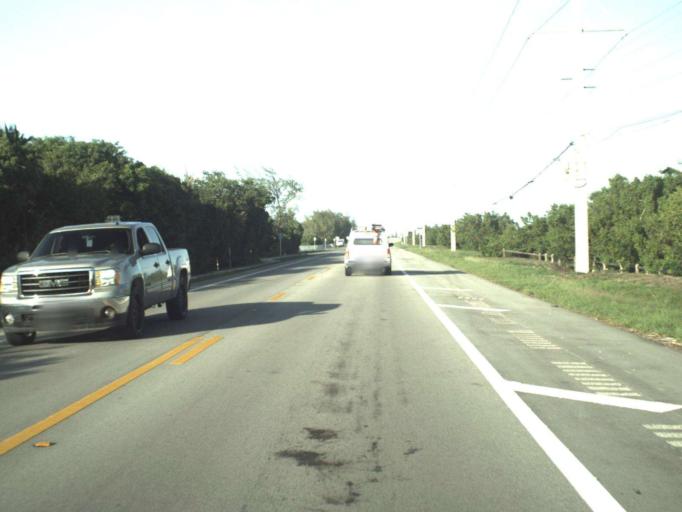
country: US
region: Florida
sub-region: Monroe County
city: Islamorada
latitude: 24.8374
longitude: -80.7604
